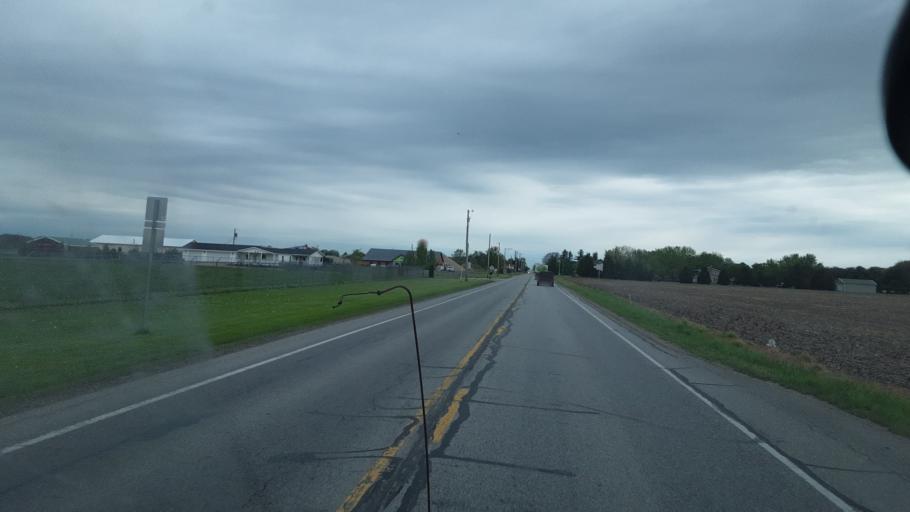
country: US
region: Indiana
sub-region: Elkhart County
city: New Paris
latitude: 41.5264
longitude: -85.7798
